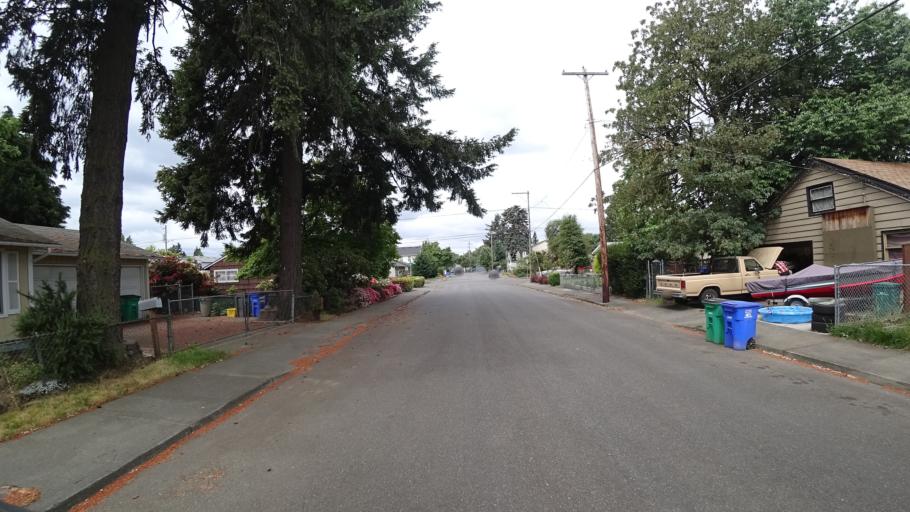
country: US
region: Oregon
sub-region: Multnomah County
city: Lents
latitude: 45.4760
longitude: -122.5670
